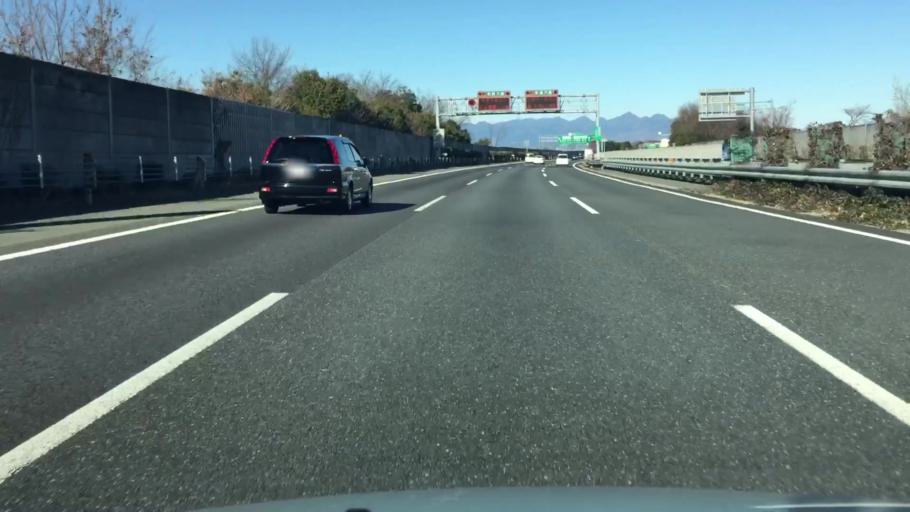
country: JP
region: Gunma
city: Fujioka
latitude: 36.2628
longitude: 139.1014
